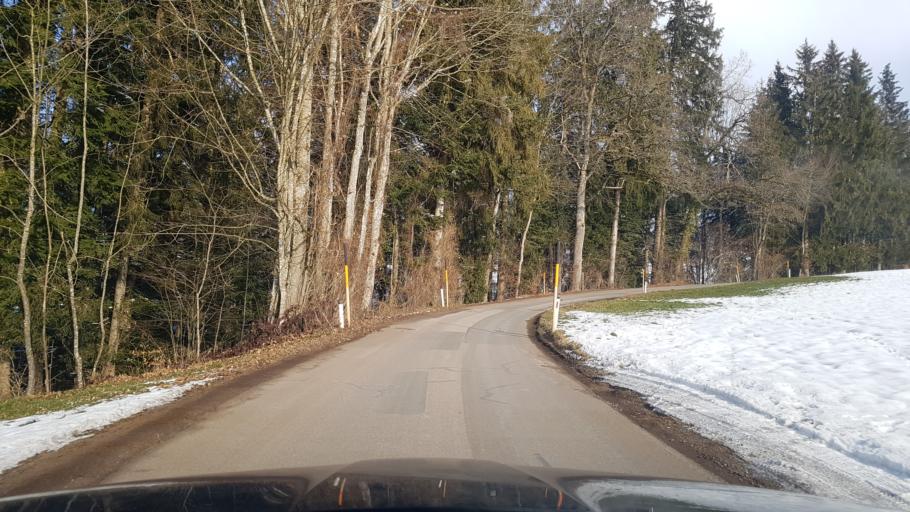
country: AT
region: Salzburg
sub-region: Politischer Bezirk Salzburg-Umgebung
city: Thalgau
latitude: 47.8562
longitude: 13.2303
